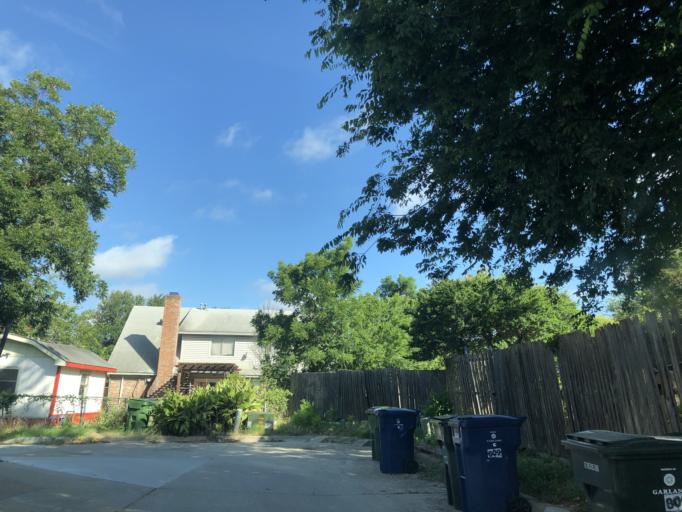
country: US
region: Texas
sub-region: Dallas County
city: Garland
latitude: 32.8585
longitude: -96.6410
